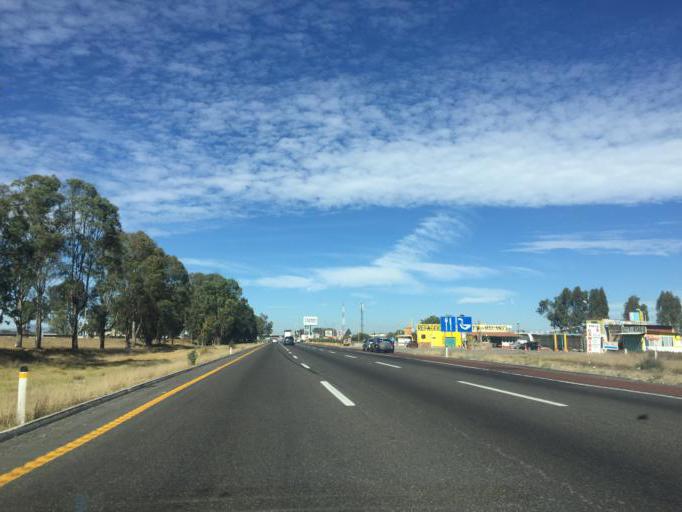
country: MX
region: Queretaro
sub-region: San Juan del Rio
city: Paso de Mata
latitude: 20.2923
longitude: -99.9220
